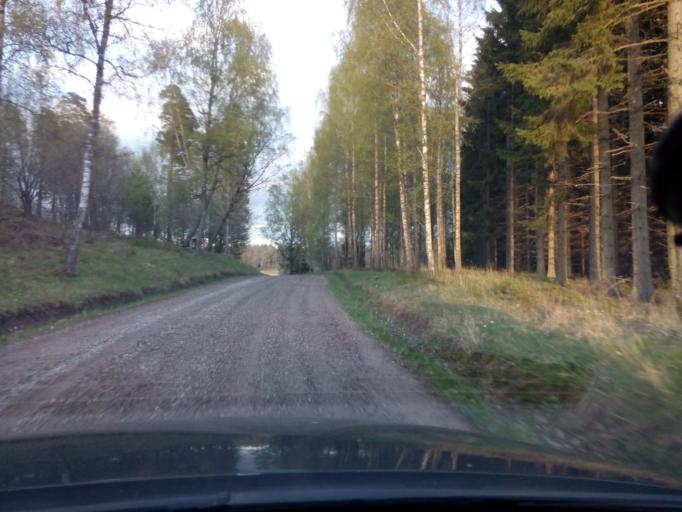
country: SE
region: Soedermanland
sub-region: Oxelosunds Kommun
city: Oxelosund
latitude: 58.7831
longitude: 17.2728
